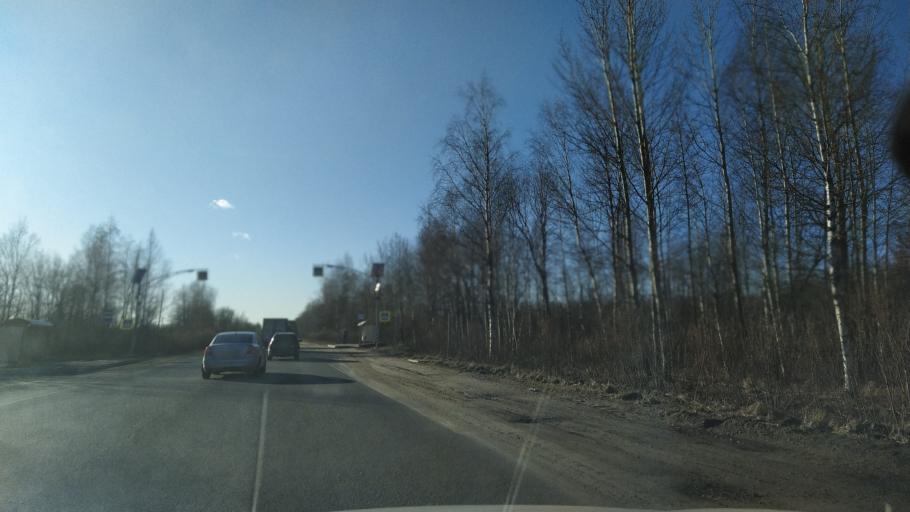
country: RU
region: St.-Petersburg
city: Gorelovo
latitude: 59.7267
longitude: 30.1804
